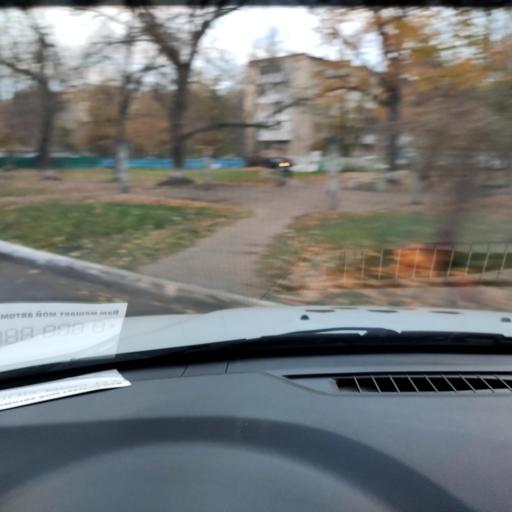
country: RU
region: Samara
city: Tol'yatti
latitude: 53.5031
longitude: 49.4079
